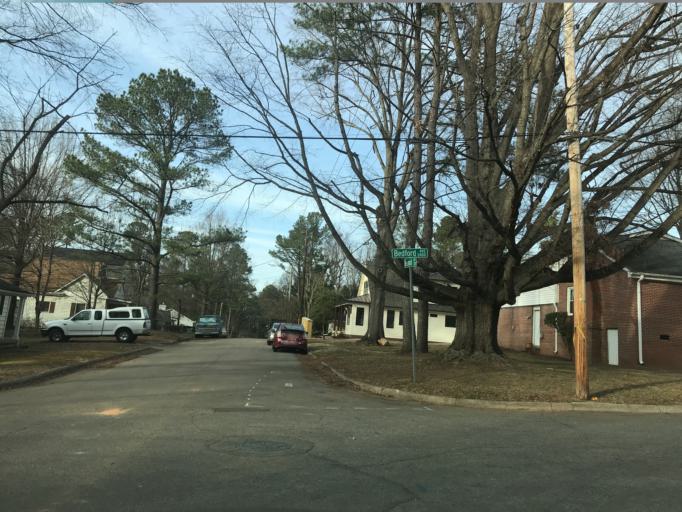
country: US
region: North Carolina
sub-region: Wake County
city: West Raleigh
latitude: 35.7937
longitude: -78.6662
